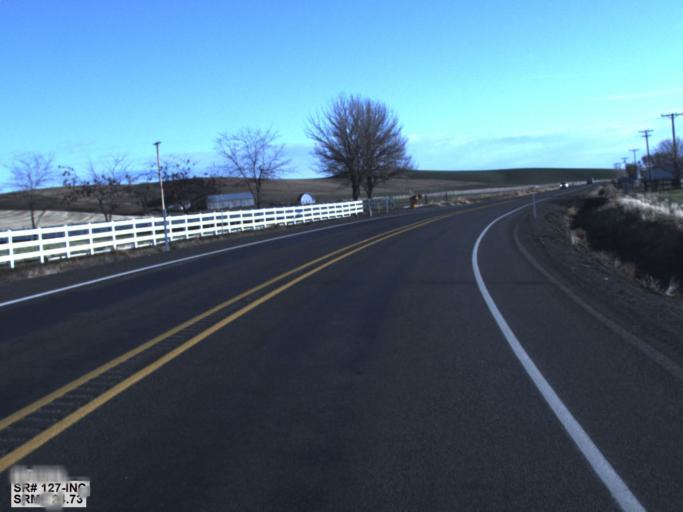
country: US
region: Washington
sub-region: Garfield County
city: Pomeroy
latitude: 46.7894
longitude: -117.6932
